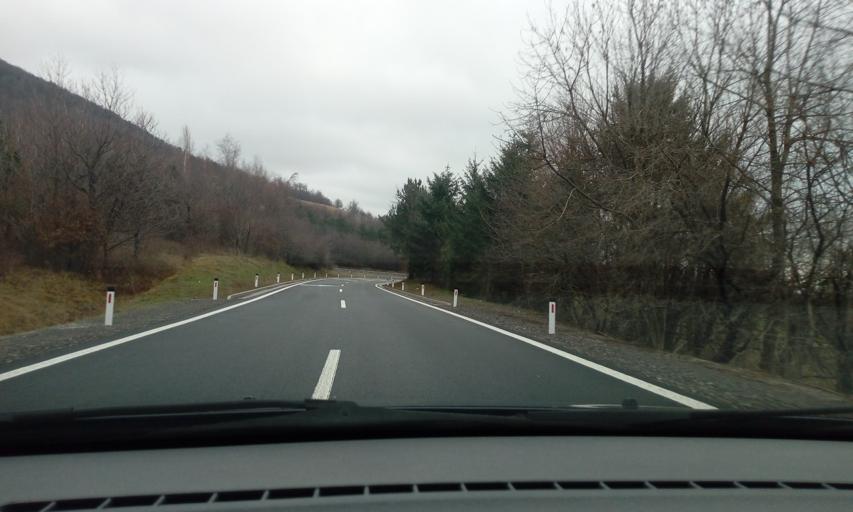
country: SI
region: Divaca
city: Divaca
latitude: 45.7583
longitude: 14.0585
